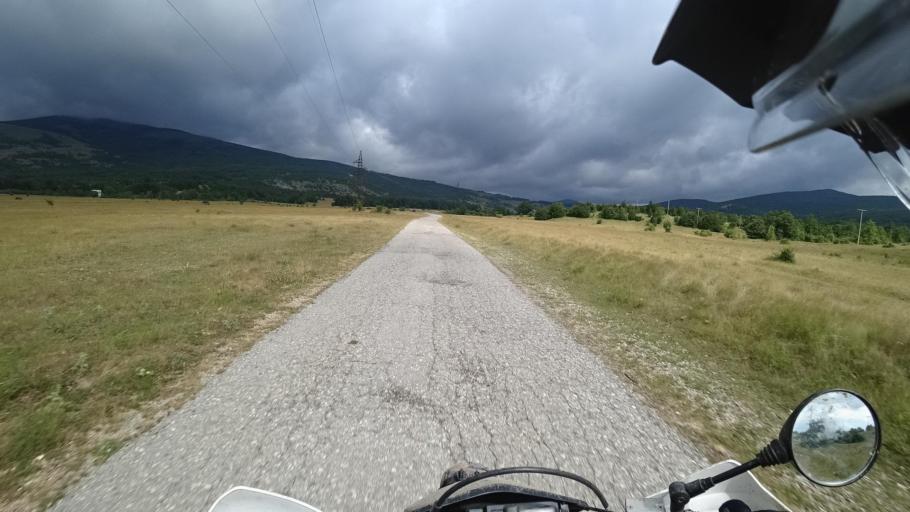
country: HR
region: Zadarska
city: Gracac
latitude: 44.5309
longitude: 15.8356
